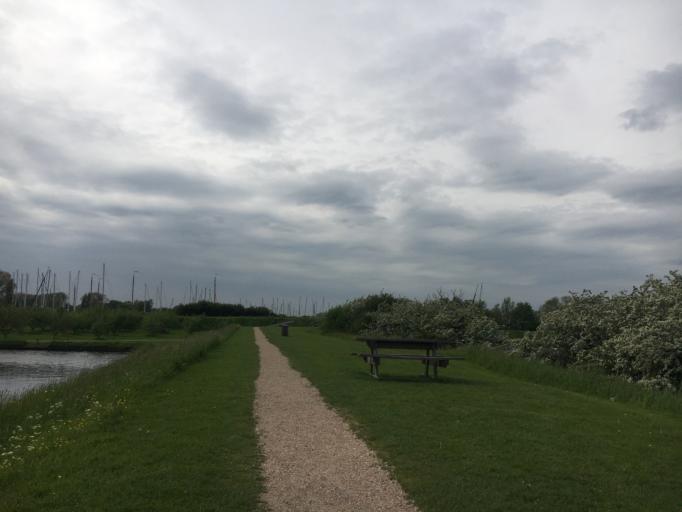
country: NL
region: North Holland
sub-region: Gemeente Weesp
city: Weesp
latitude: 52.3346
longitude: 5.0722
